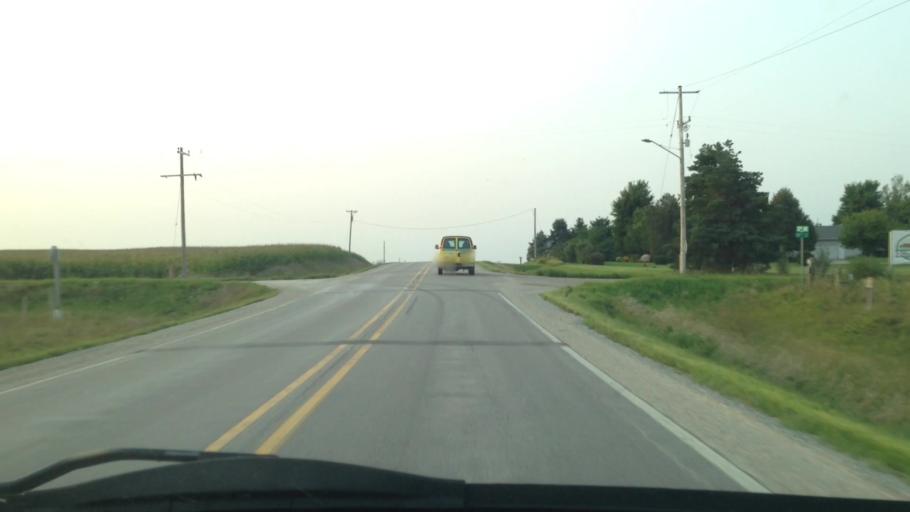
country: US
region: Iowa
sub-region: Benton County
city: Atkins
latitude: 42.0211
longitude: -91.8738
